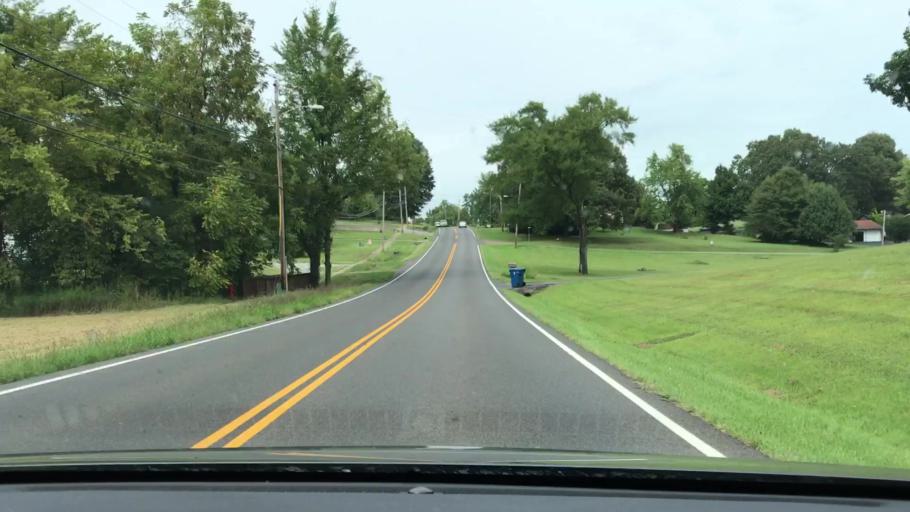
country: US
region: Kentucky
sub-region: Marshall County
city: Benton
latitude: 36.8396
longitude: -88.3505
